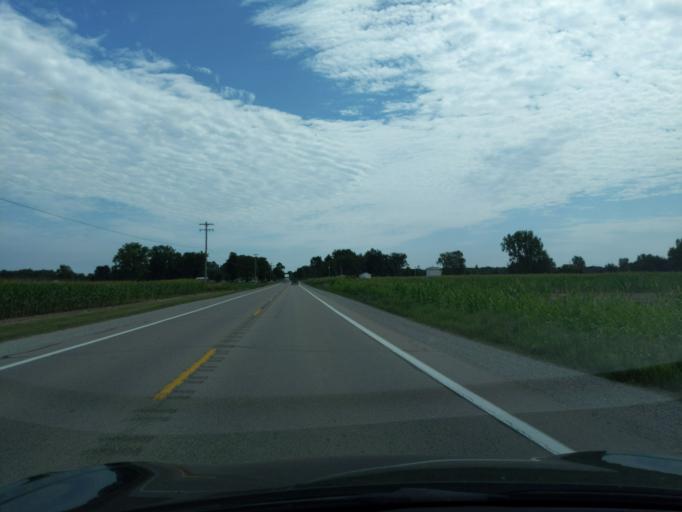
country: US
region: Michigan
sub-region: Gratiot County
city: Breckenridge
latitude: 43.4081
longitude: -84.3786
